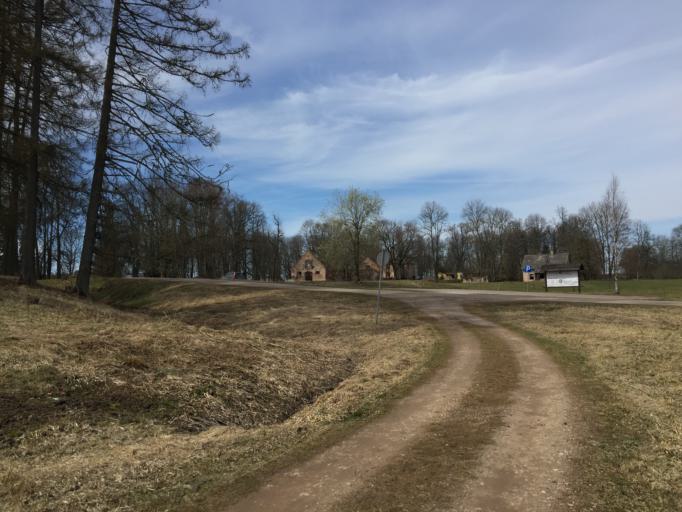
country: LV
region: Strenci
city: Seda
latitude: 57.8132
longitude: 25.8312
